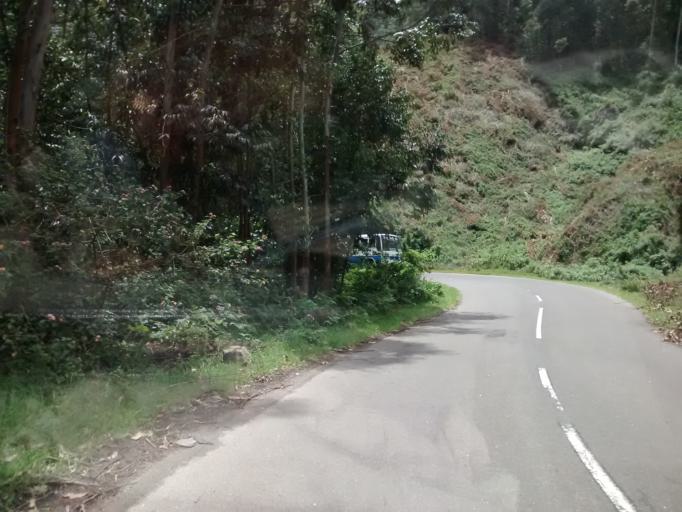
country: IN
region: Kerala
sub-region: Idukki
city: Munnar
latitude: 10.1240
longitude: 77.1598
